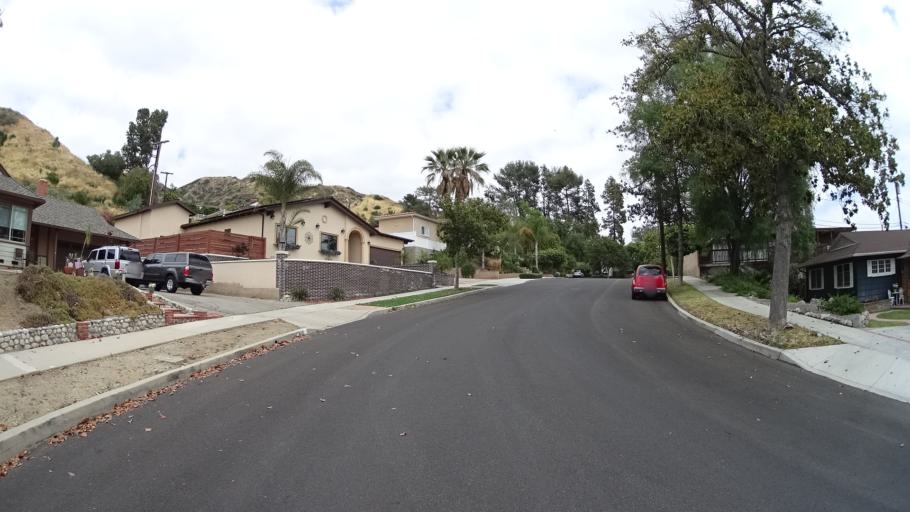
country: US
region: California
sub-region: Los Angeles County
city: Burbank
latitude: 34.2047
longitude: -118.3211
